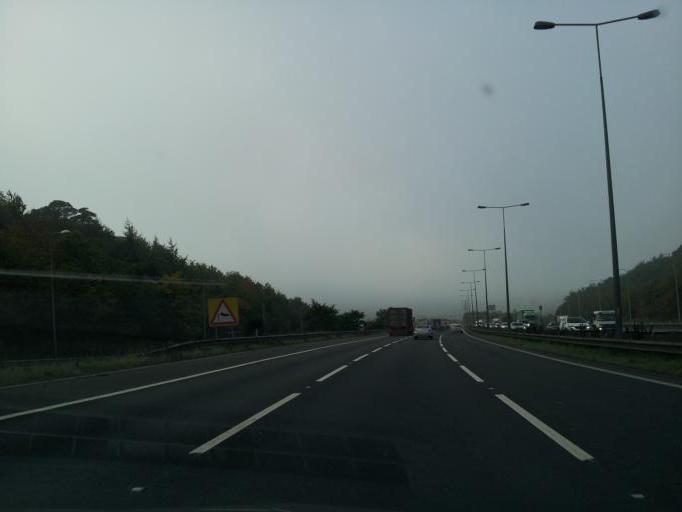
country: GB
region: England
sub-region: Calderdale
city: Brighouse
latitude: 53.6985
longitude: -1.7469
